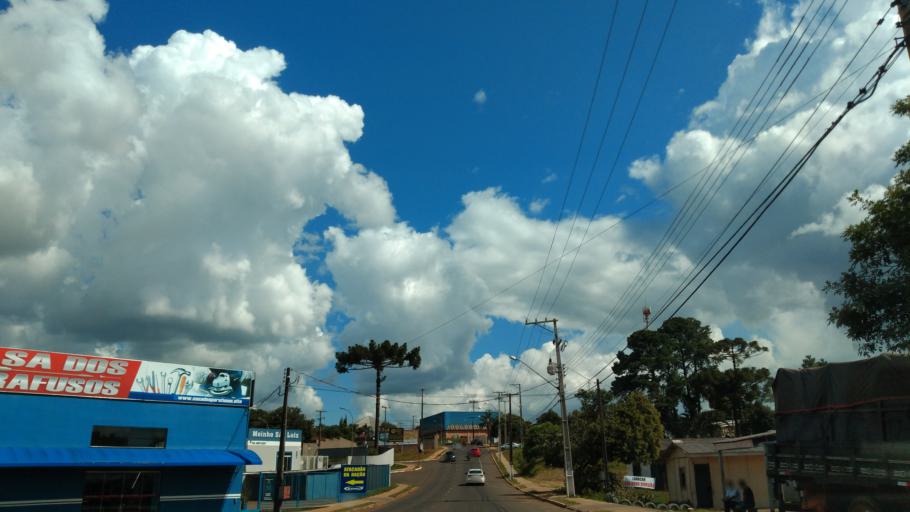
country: BR
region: Parana
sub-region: Guarapuava
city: Guarapuava
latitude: -25.3962
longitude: -51.4933
